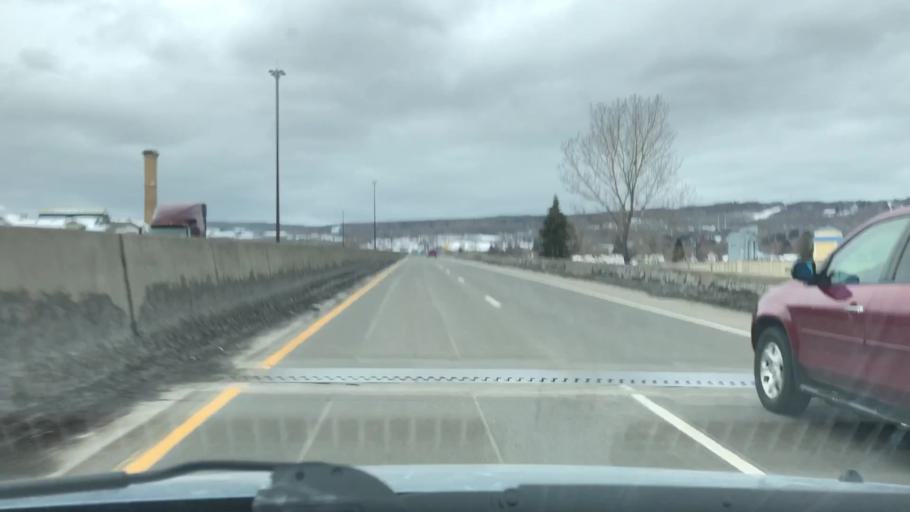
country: US
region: Minnesota
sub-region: Saint Louis County
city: Proctor
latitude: 46.7361
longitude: -92.1664
